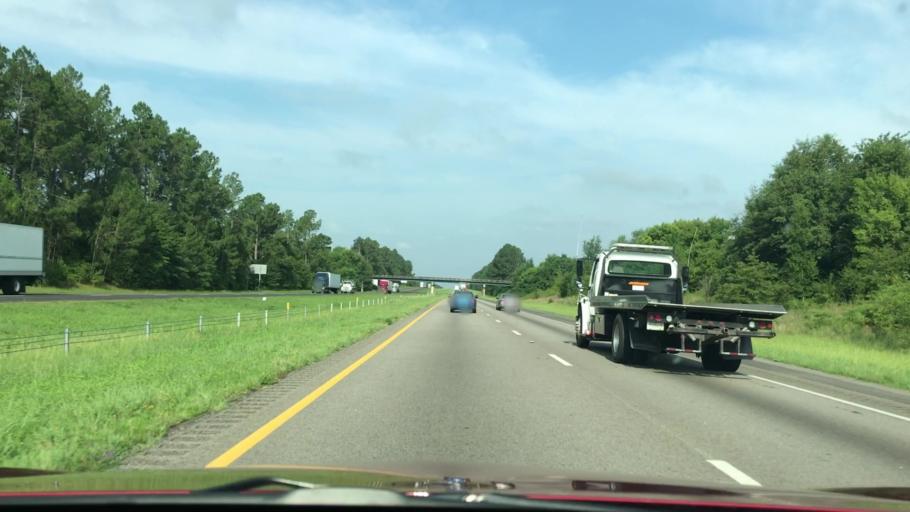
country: US
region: South Carolina
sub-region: Aiken County
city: Aiken
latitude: 33.6359
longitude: -81.7584
